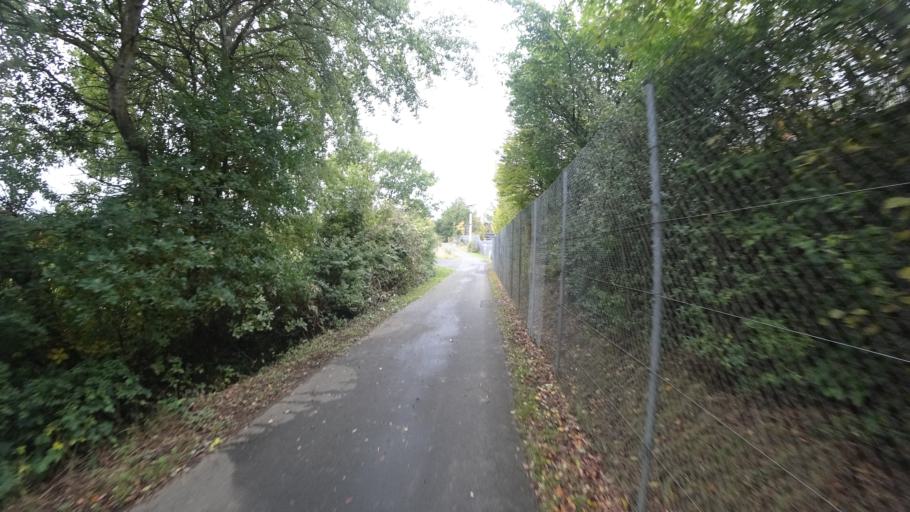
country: DE
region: Rheinland-Pfalz
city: Selters
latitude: 50.5395
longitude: 7.7490
